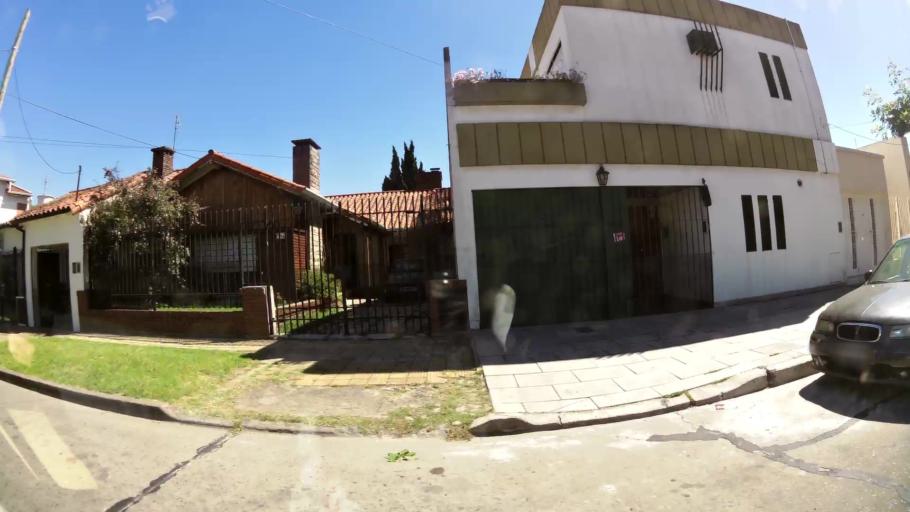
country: AR
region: Buenos Aires
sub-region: Partido de General San Martin
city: General San Martin
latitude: -34.5284
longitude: -58.5329
